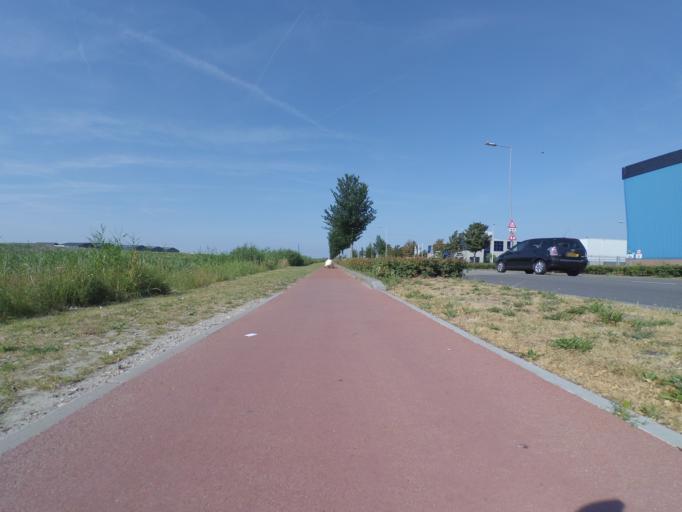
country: NL
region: North Brabant
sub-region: Gemeente Bergen op Zoom
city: Bergen op Zoom
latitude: 51.4965
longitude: 4.2672
